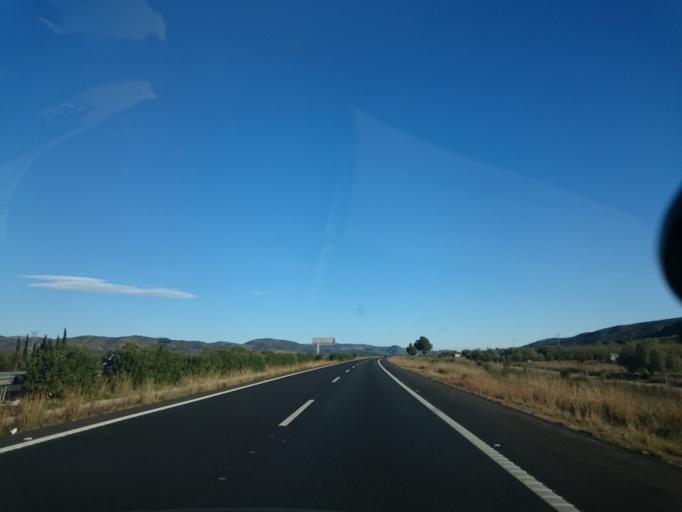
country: ES
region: Valencia
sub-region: Provincia de Castello
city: Alcala de Xivert
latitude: 40.3075
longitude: 0.2401
